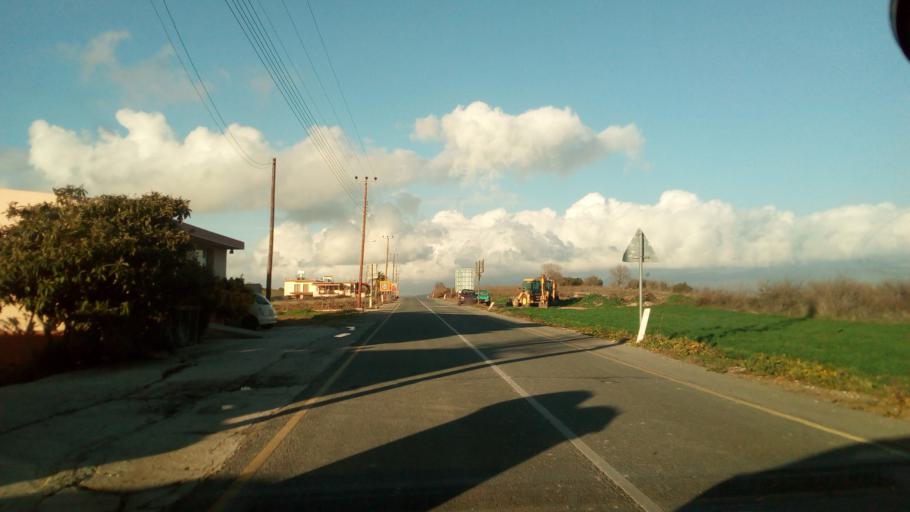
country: CY
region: Pafos
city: Mesogi
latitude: 34.8522
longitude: 32.4947
